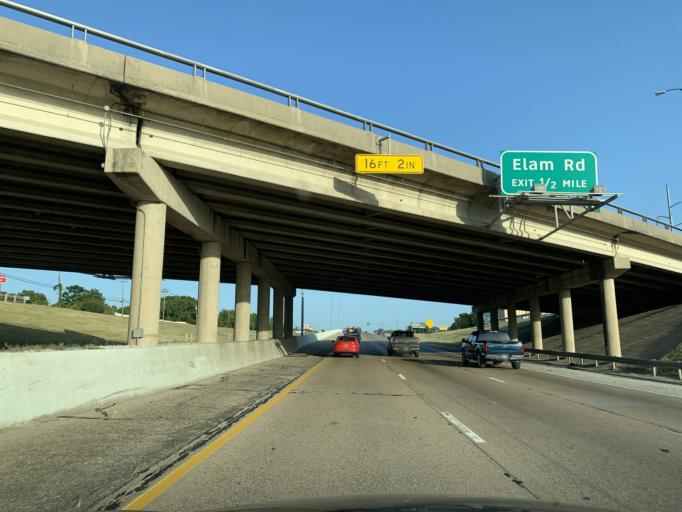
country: US
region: Texas
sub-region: Dallas County
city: Hutchins
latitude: 32.7246
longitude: -96.7006
